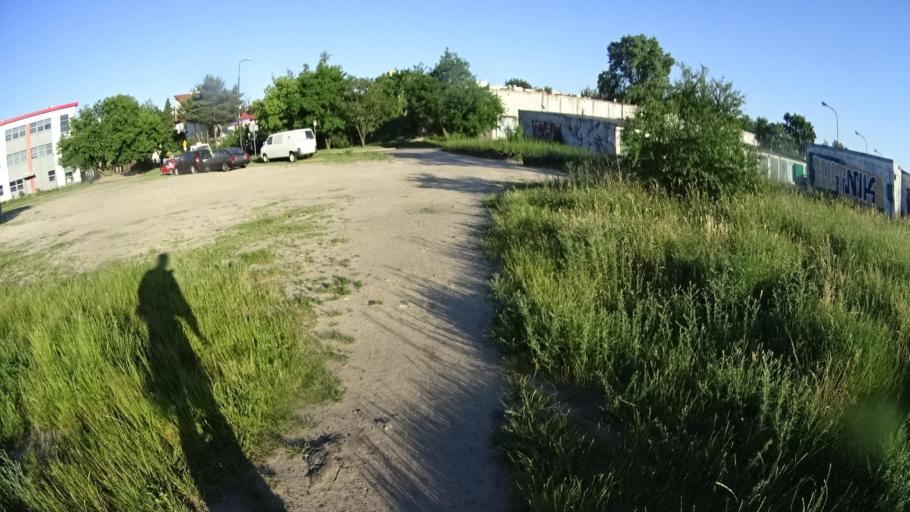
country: PL
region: Masovian Voivodeship
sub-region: Warszawa
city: Bemowo
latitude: 52.2596
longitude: 20.9147
